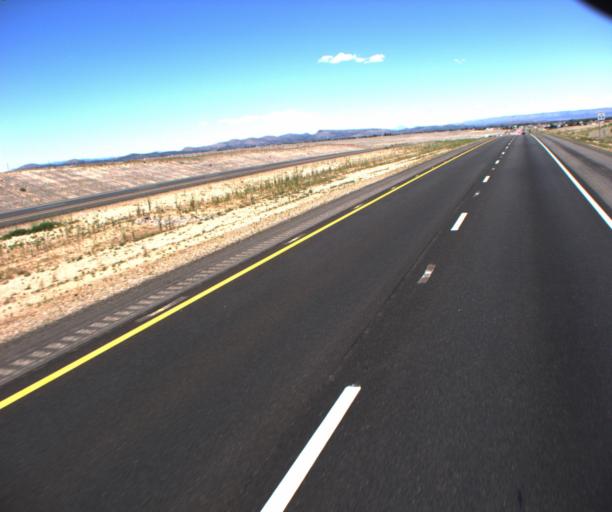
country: US
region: Arizona
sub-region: Yavapai County
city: Chino Valley
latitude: 34.6951
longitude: -112.4474
